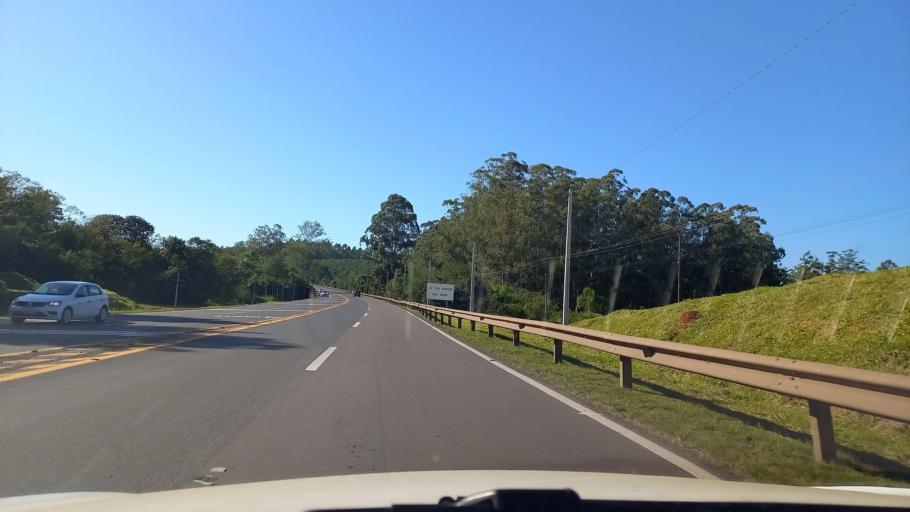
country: BR
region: Rio Grande do Sul
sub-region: Montenegro
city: Montenegro
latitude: -29.8197
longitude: -51.4506
